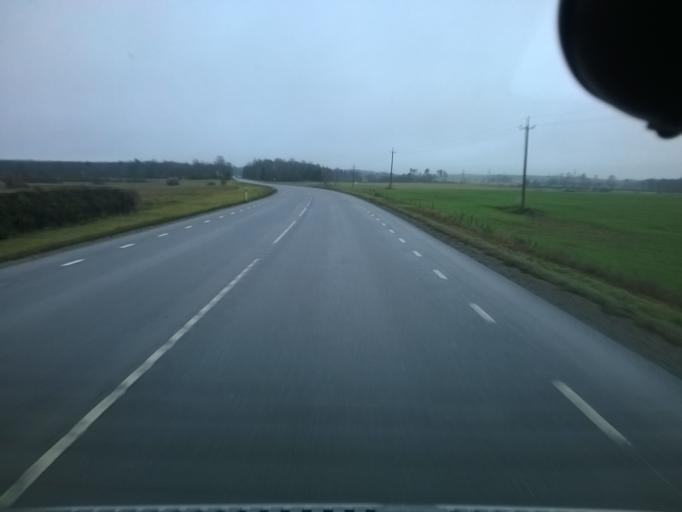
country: EE
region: Harju
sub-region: Saku vald
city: Saku
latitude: 59.2851
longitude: 24.7411
